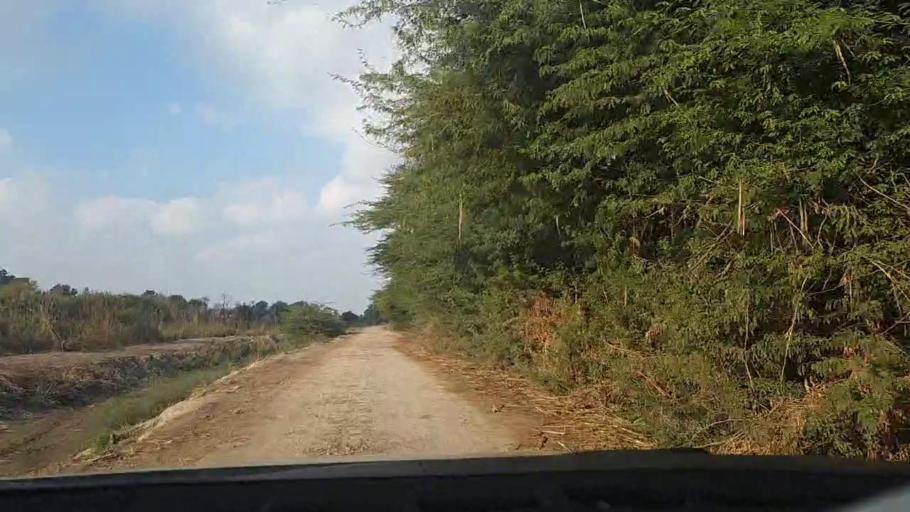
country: PK
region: Sindh
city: Tando Mittha Khan
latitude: 25.9143
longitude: 69.3039
